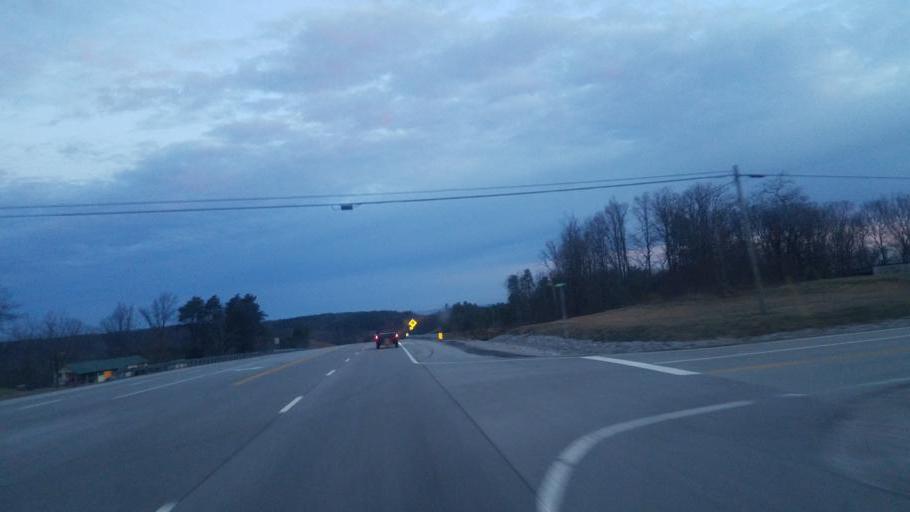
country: US
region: Tennessee
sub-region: Van Buren County
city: Spencer
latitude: 35.7587
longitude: -85.4595
